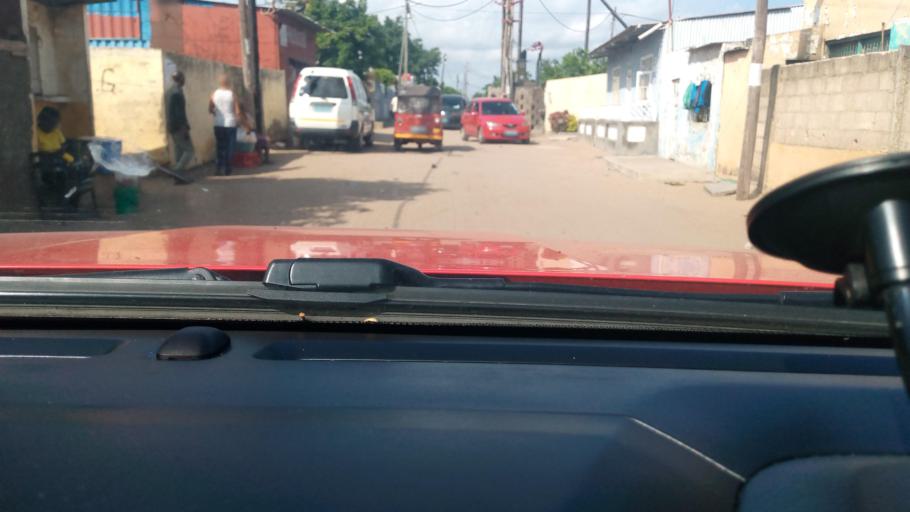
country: MZ
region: Maputo City
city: Maputo
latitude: -25.9158
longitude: 32.5629
